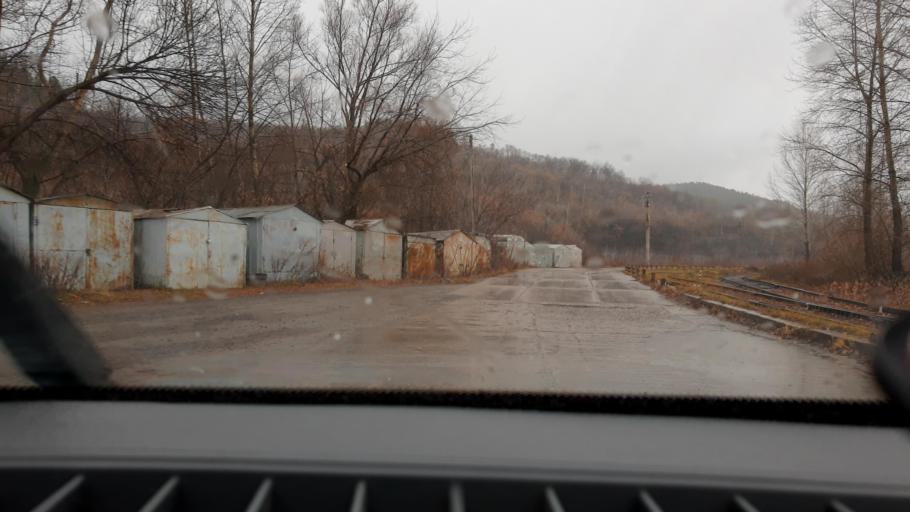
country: RU
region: Bashkortostan
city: Ufa
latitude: 54.7639
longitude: 55.9803
